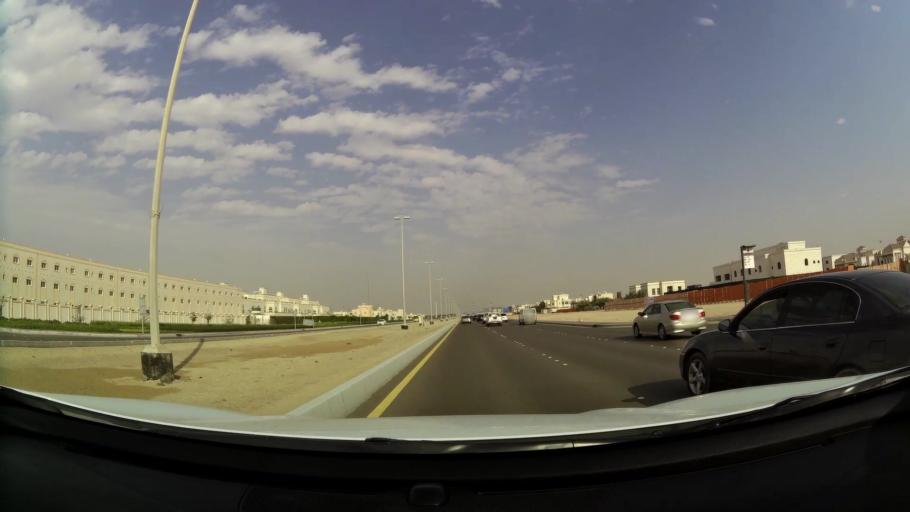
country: AE
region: Abu Dhabi
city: Abu Dhabi
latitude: 24.3257
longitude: 54.5652
